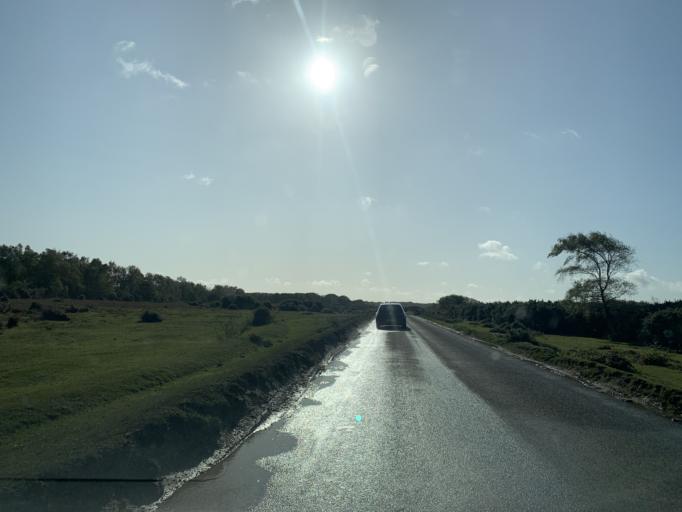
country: GB
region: England
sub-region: Wiltshire
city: Downton
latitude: 50.9599
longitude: -1.6980
